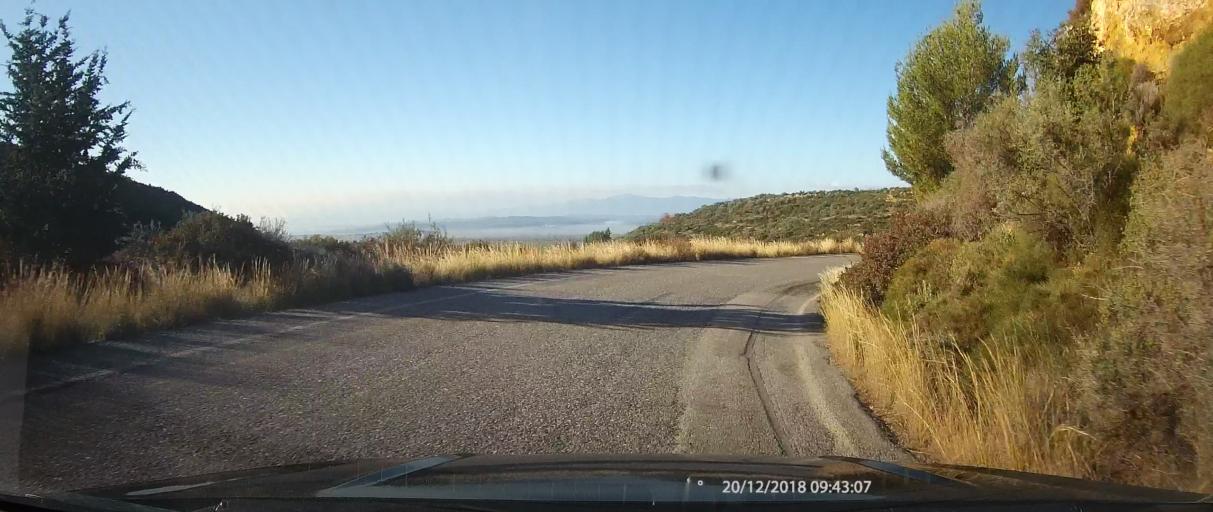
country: GR
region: Peloponnese
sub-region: Nomos Lakonias
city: Yerakion
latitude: 36.9626
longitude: 22.7472
